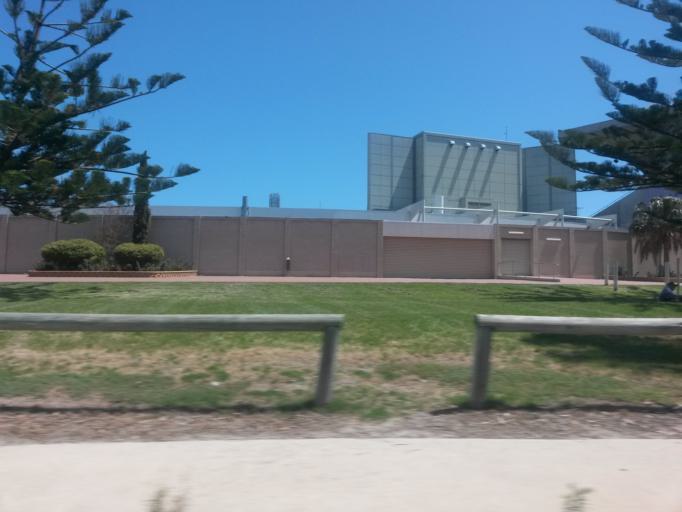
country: AU
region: South Australia
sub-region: Charles Sturt
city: Royal Park
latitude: -34.8786
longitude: 138.4966
